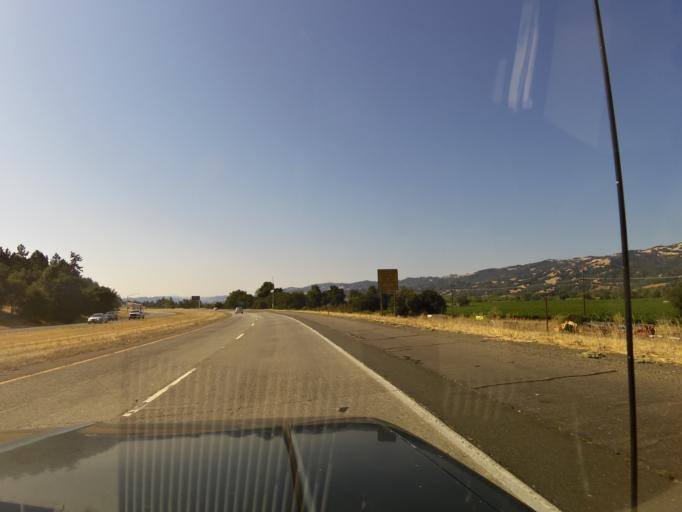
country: US
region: California
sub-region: Sonoma County
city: Healdsburg
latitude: 38.6919
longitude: -122.8831
